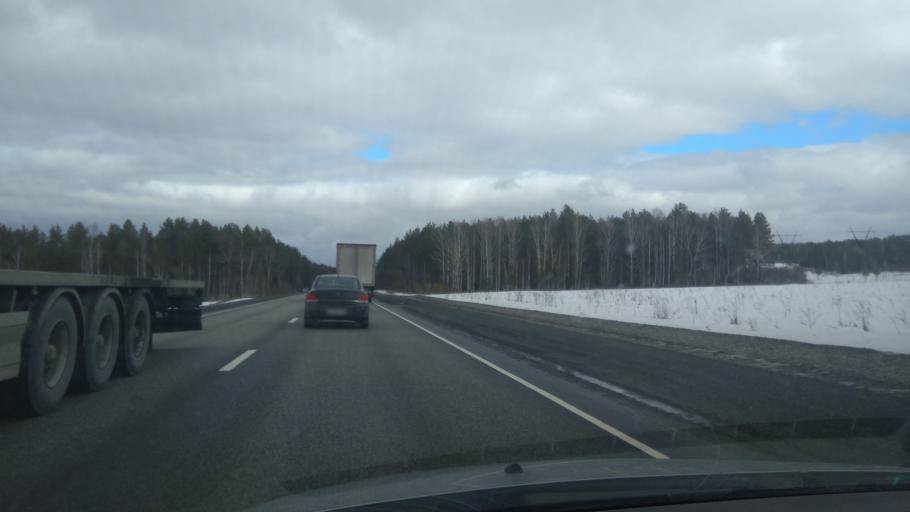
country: RU
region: Sverdlovsk
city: Bisert'
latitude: 56.8251
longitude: 58.7671
